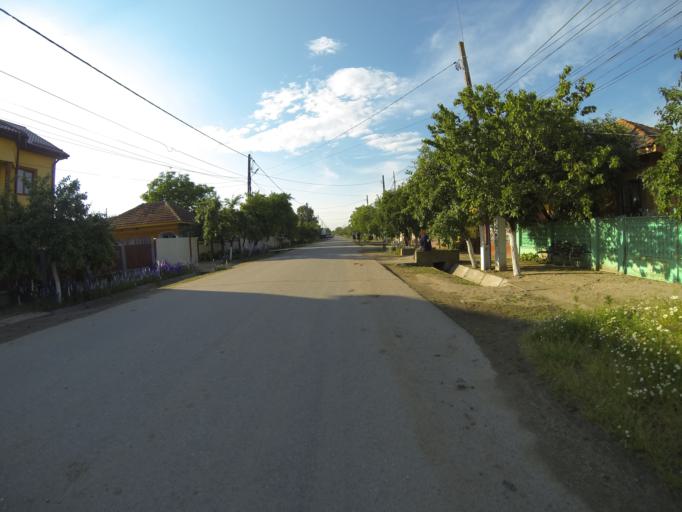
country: RO
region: Dolj
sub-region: Comuna Tuglui
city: Tuglui
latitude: 44.1815
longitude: 23.8147
